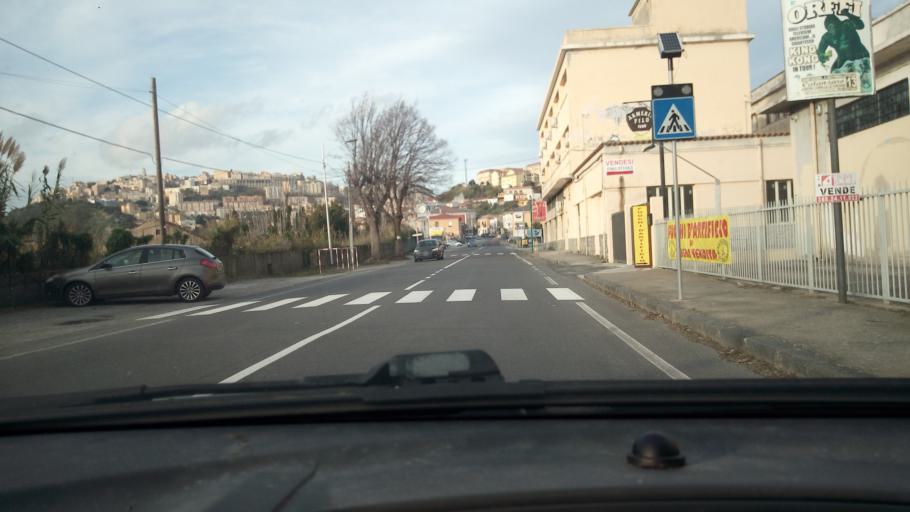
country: IT
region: Calabria
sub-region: Provincia di Catanzaro
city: Catanzaro
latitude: 38.8882
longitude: 16.6026
